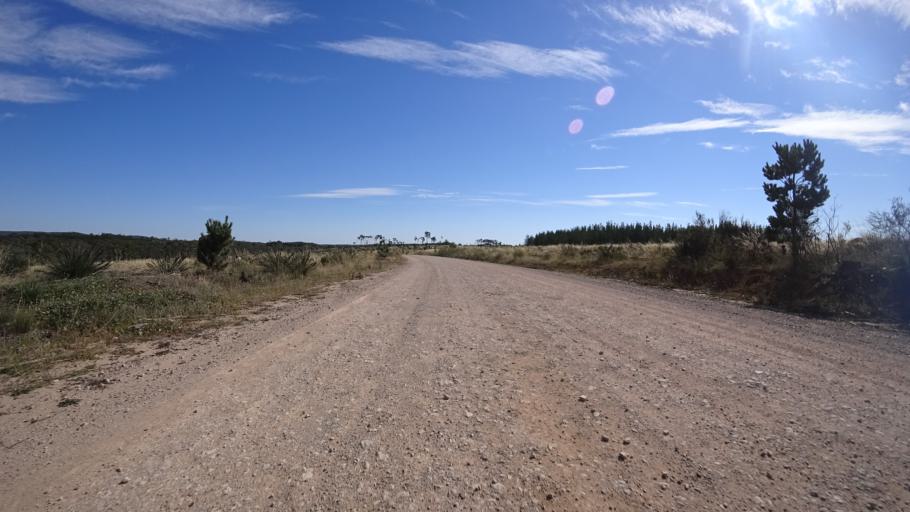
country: AU
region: New South Wales
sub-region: Lithgow
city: Lithgow
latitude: -33.3770
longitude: 150.2436
